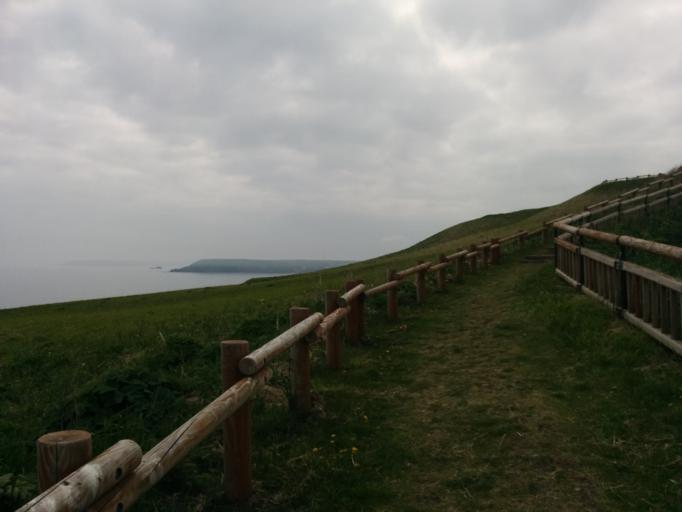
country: JP
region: Hokkaido
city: Nemuro
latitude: 43.0765
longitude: 145.1710
